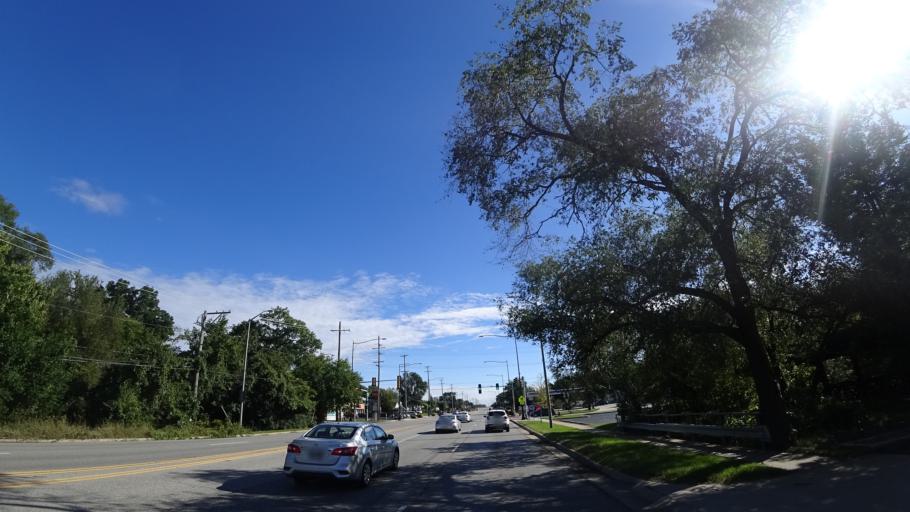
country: US
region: Illinois
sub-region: Cook County
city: Oak Forest
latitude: 41.6187
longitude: -87.7371
